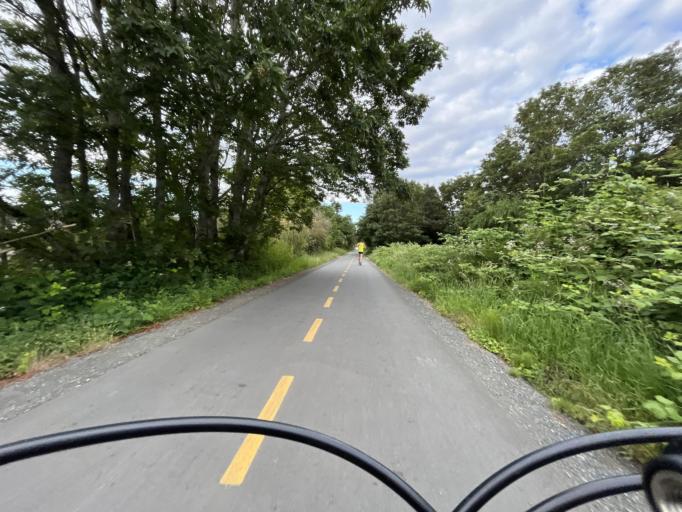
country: CA
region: British Columbia
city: Victoria
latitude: 48.4620
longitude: -123.3697
